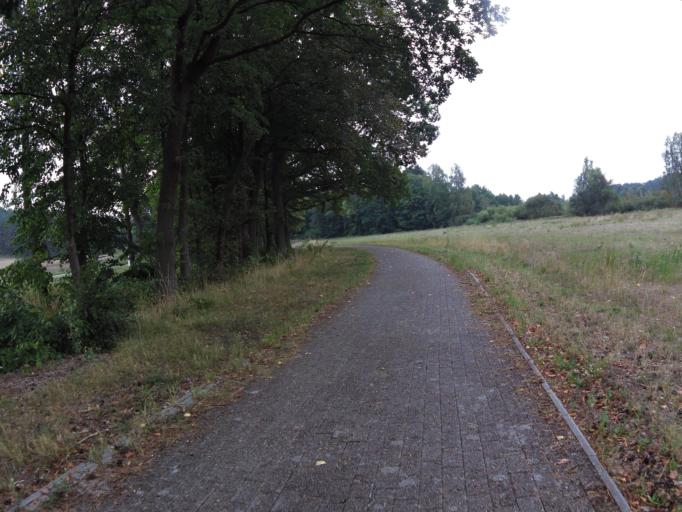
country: DE
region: Mecklenburg-Vorpommern
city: Seebad Heringsdorf
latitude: 53.8903
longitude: 14.1669
